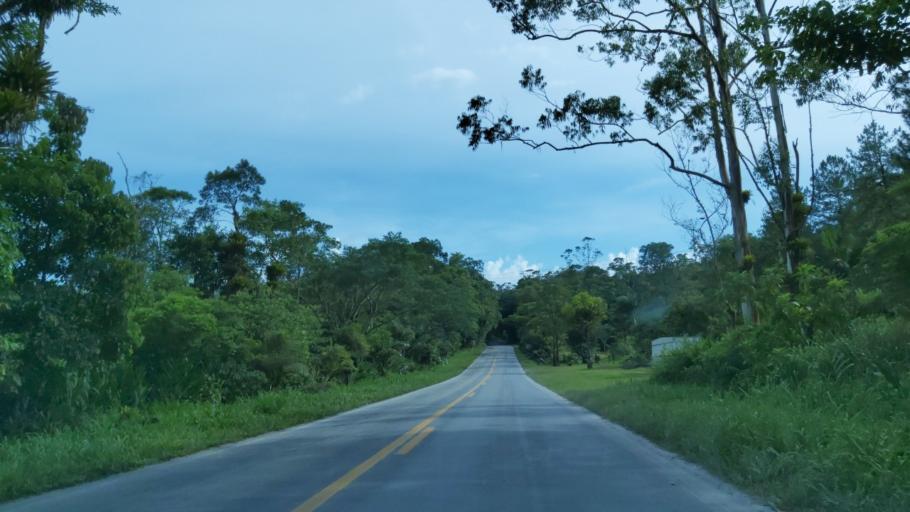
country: BR
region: Sao Paulo
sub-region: Miracatu
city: Miracatu
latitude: -24.0595
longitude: -47.5883
